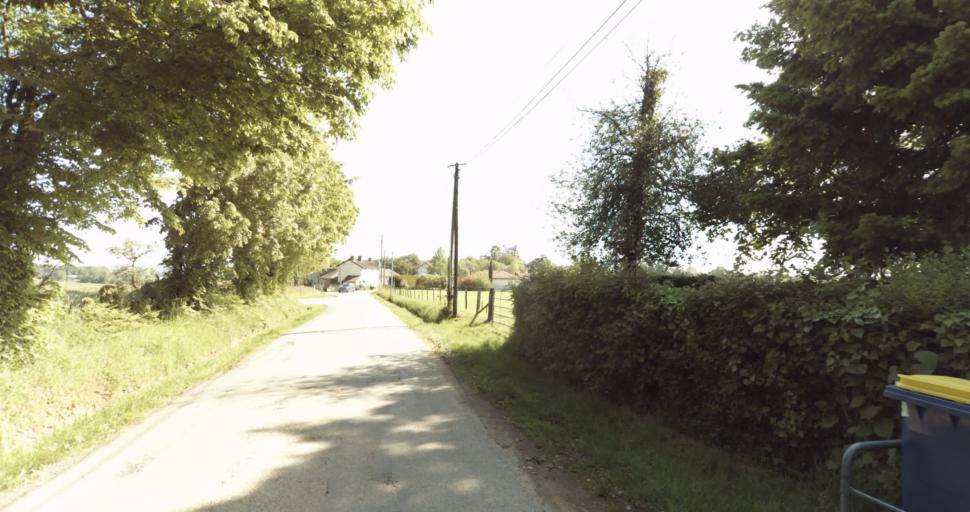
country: FR
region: Limousin
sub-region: Departement de la Haute-Vienne
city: Solignac
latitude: 45.7191
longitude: 1.2668
